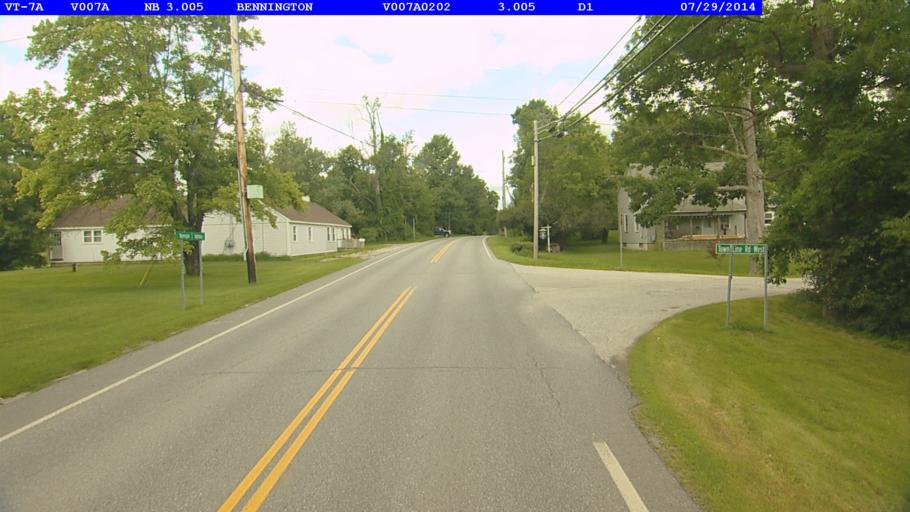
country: US
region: Vermont
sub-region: Bennington County
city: North Bennington
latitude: 42.9325
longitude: -73.2100
